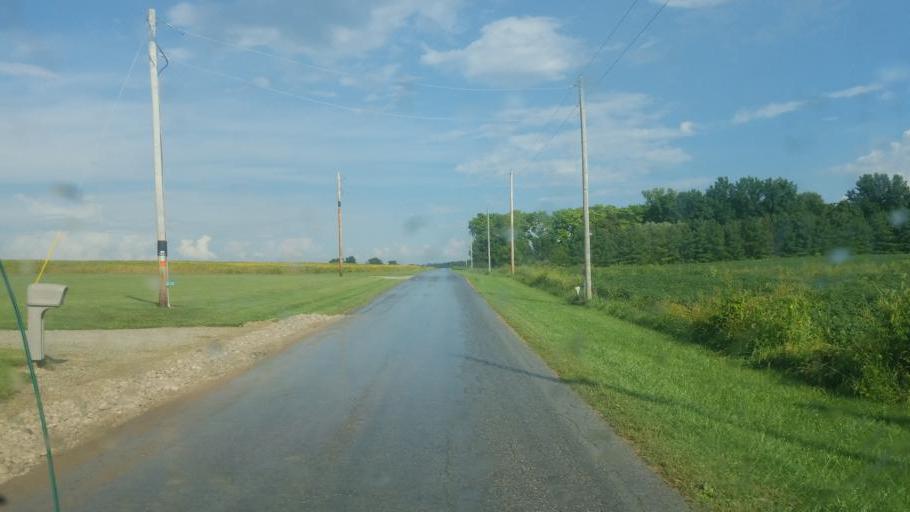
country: US
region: Ohio
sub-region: Huron County
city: Plymouth
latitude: 41.0077
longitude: -82.5953
